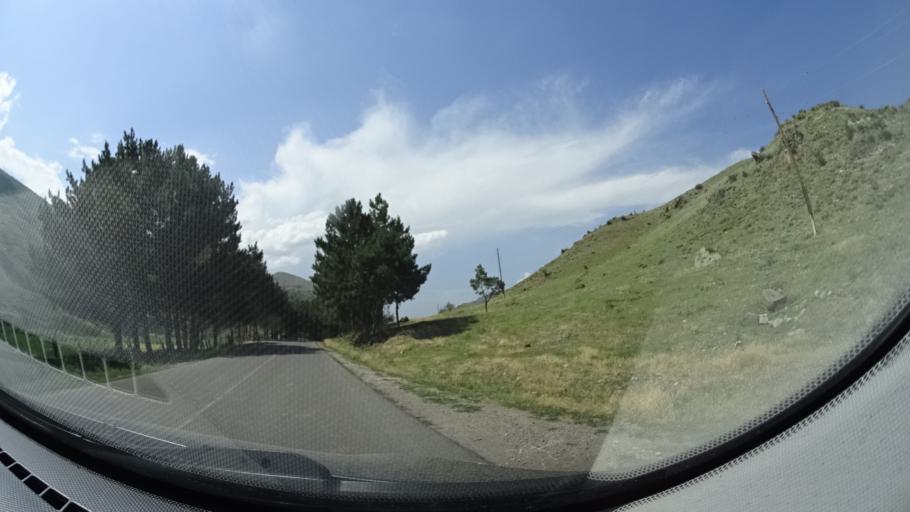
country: GE
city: Akhalk'alak'i
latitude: 41.4209
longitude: 43.3239
